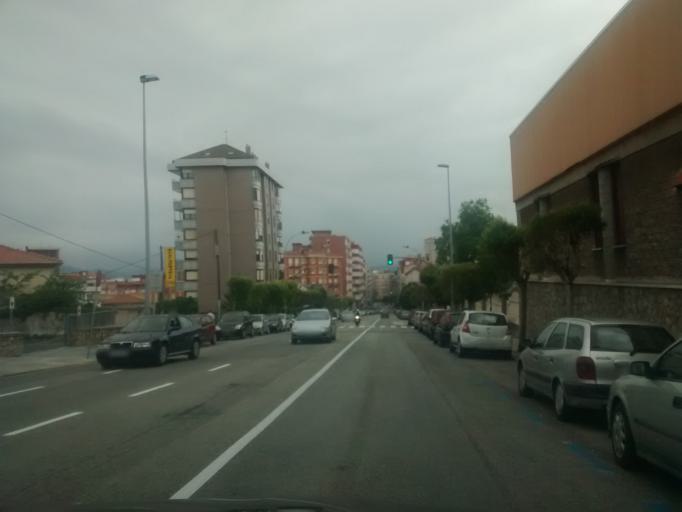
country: ES
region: Cantabria
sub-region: Provincia de Cantabria
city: Santander
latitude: 43.4632
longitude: -3.8230
